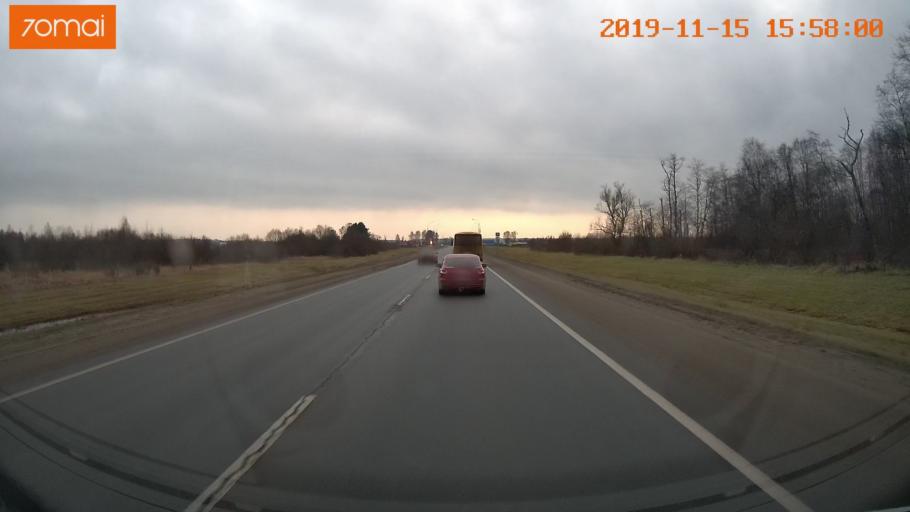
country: RU
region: Jaroslavl
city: Yaroslavl
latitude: 57.8247
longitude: 39.9587
